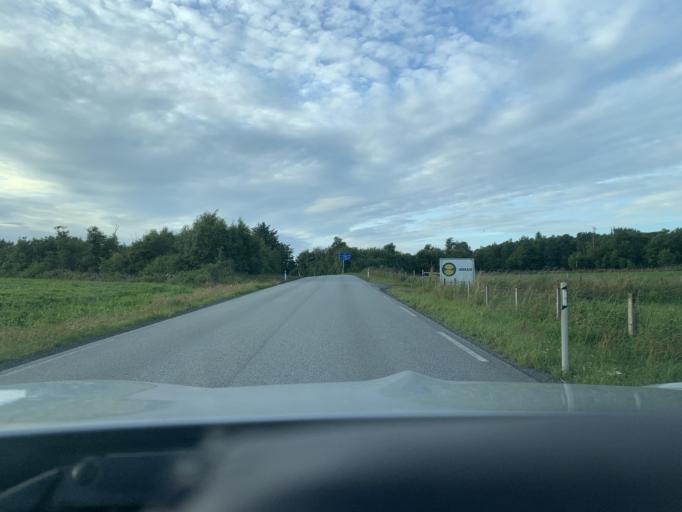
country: NO
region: Rogaland
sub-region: Time
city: Bryne
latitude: 58.6966
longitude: 5.7103
